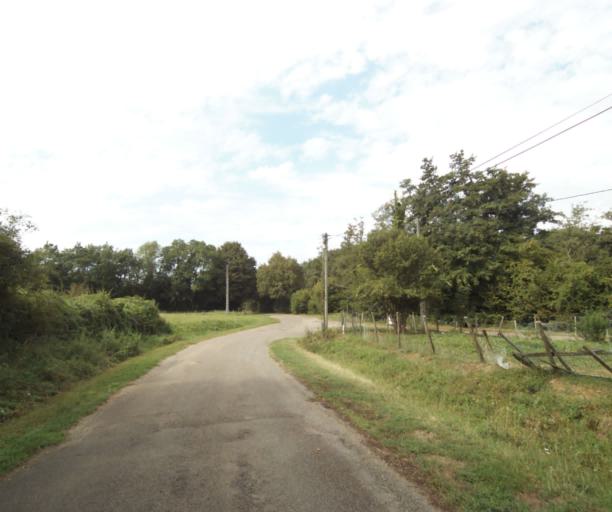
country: FR
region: Bourgogne
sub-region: Departement de Saone-et-Loire
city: Tournus
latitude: 46.5479
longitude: 4.9092
